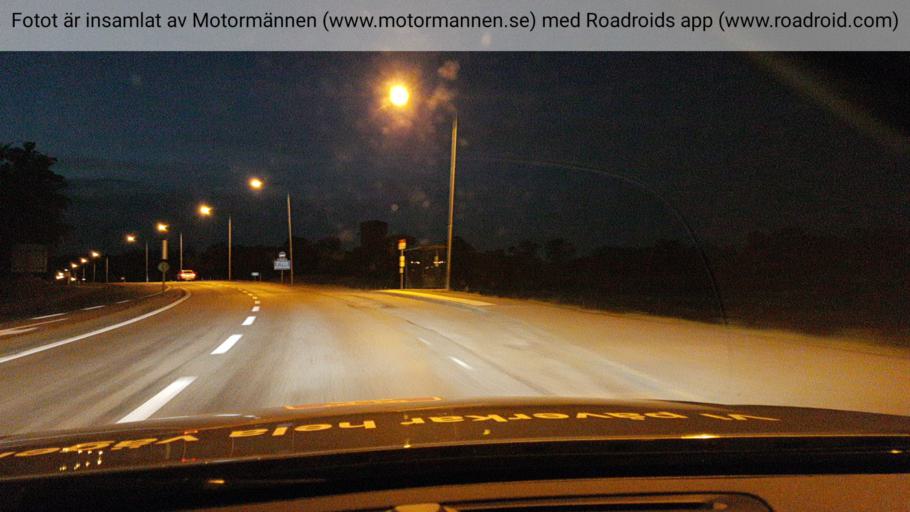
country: SE
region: Stockholm
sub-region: Ekero Kommun
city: Ekeroe
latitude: 59.3204
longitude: 17.8677
